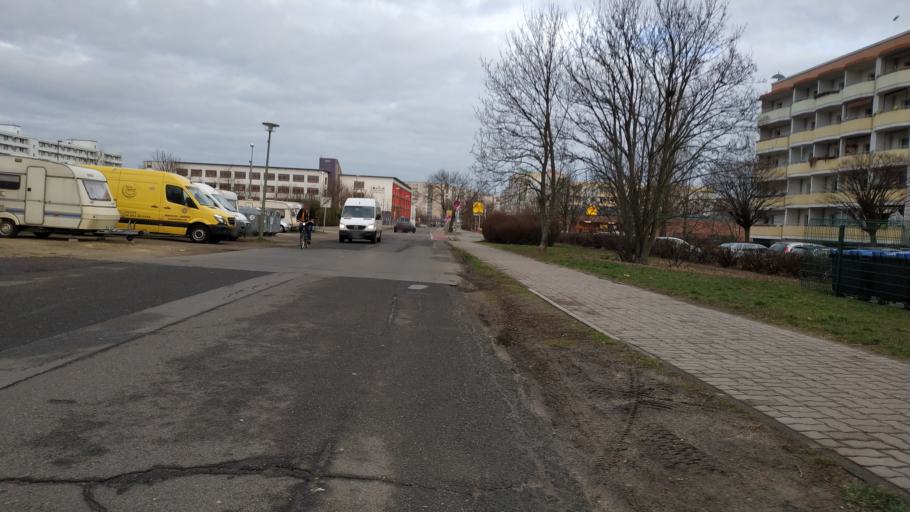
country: DE
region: Berlin
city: Hellersdorf
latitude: 52.5409
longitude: 13.5918
